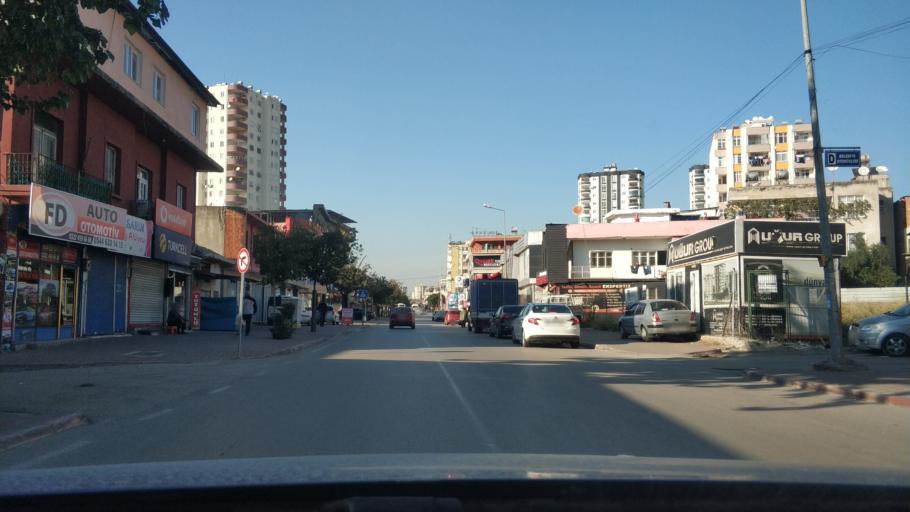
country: TR
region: Adana
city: Seyhan
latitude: 37.0099
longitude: 35.3068
